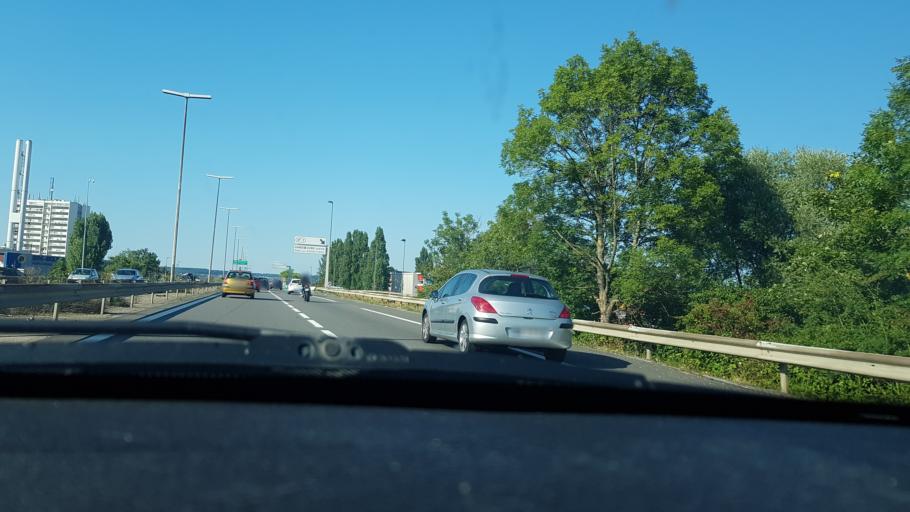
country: FR
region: Lorraine
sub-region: Departement de Meurthe-et-Moselle
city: Vandoeuvre-les-Nancy
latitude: 48.6578
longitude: 6.1857
